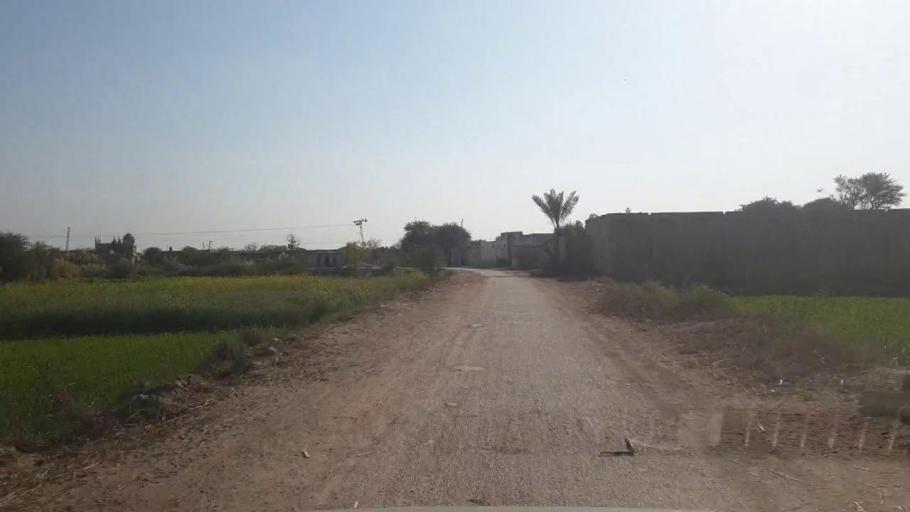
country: PK
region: Sindh
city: Chambar
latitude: 25.2894
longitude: 68.8528
